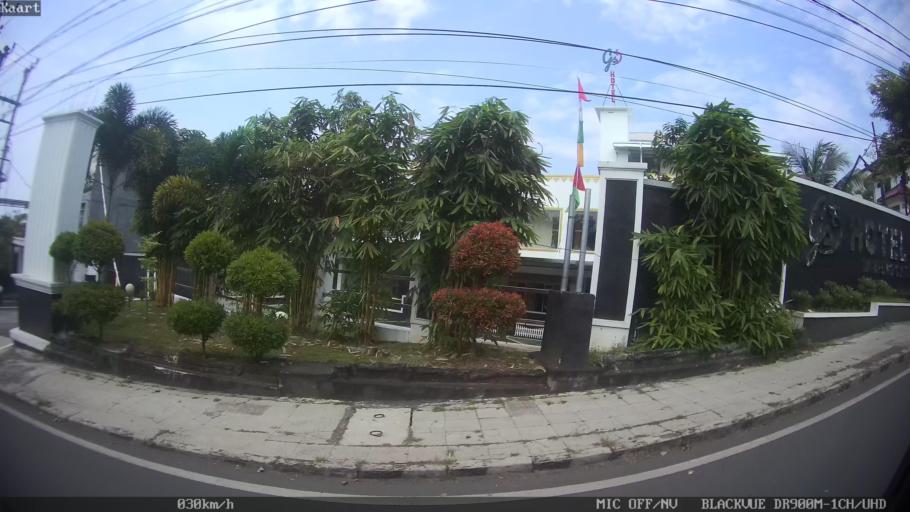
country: ID
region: Lampung
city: Bandarlampung
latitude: -5.4283
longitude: 105.2519
